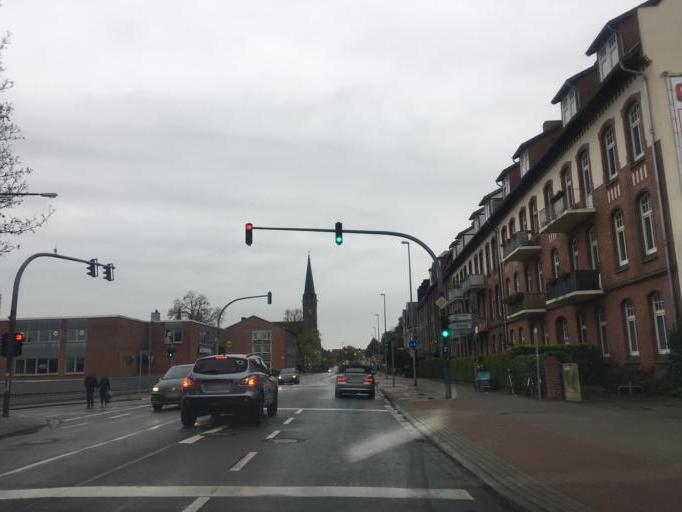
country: DE
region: Lower Saxony
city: Lueneburg
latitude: 53.2556
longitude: 10.4100
